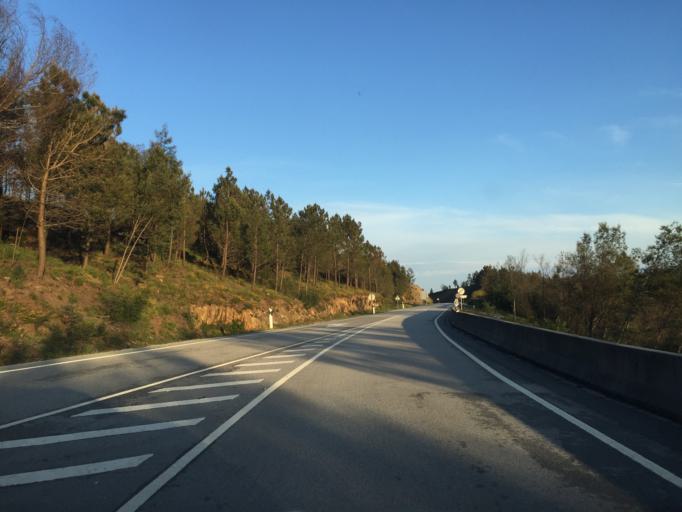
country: PT
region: Coimbra
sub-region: Pampilhosa da Serra
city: Pampilhosa da Serra
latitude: 40.1102
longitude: -8.0153
